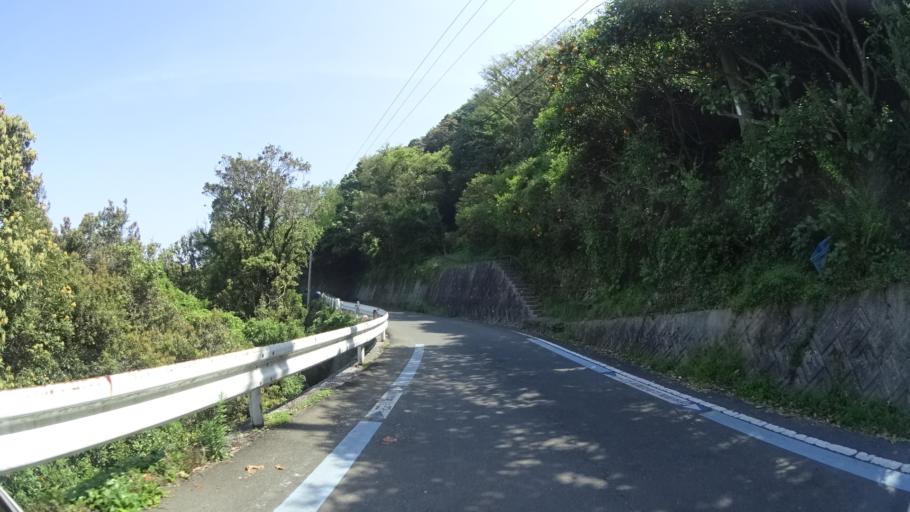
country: JP
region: Oita
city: Tsukumiura
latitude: 33.3512
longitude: 132.0297
